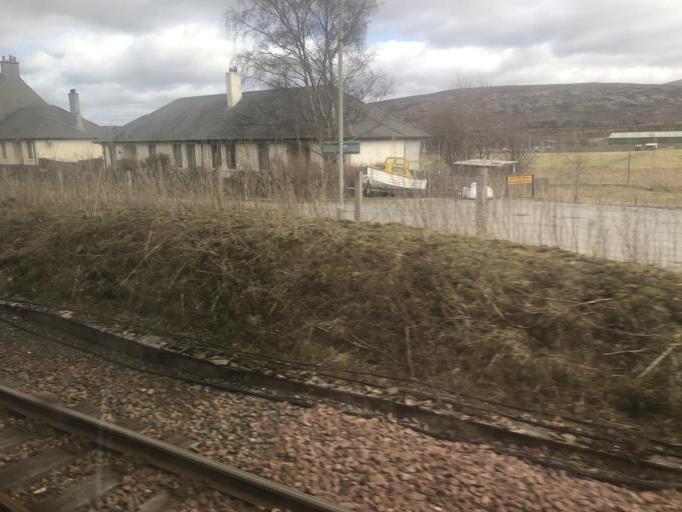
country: GB
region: Scotland
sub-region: Highland
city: Kingussie
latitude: 56.9332
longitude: -4.2474
